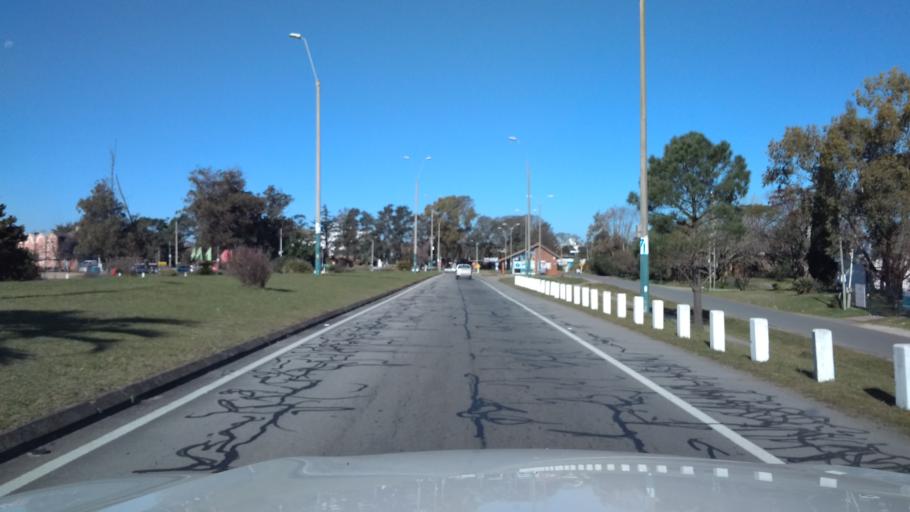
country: UY
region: Canelones
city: Atlantida
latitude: -34.7683
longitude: -55.7652
